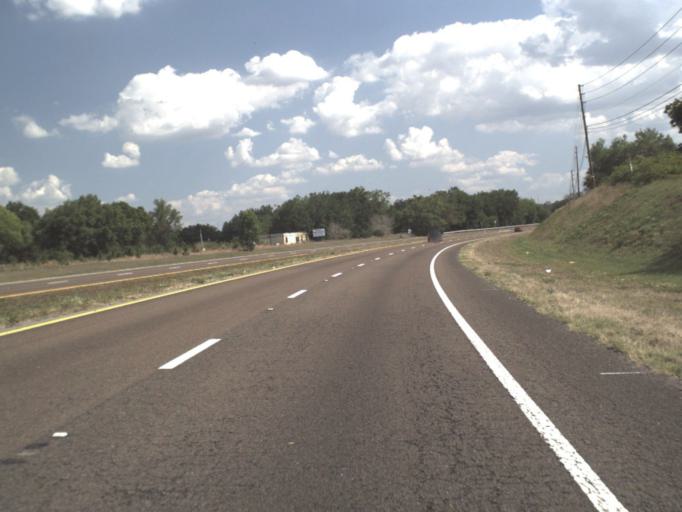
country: US
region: Florida
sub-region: Lake County
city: Minneola
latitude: 28.6253
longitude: -81.7623
